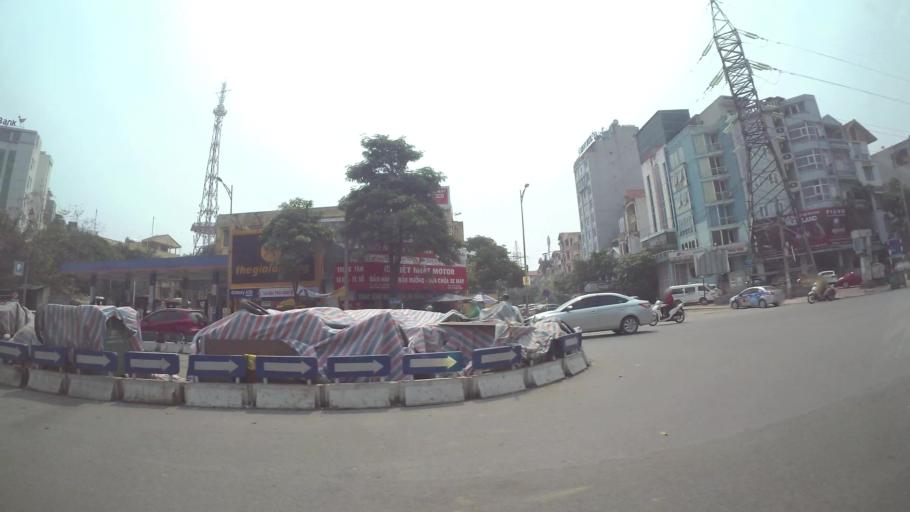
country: VN
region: Ha Noi
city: Dong Da
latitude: 21.0265
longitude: 105.8276
